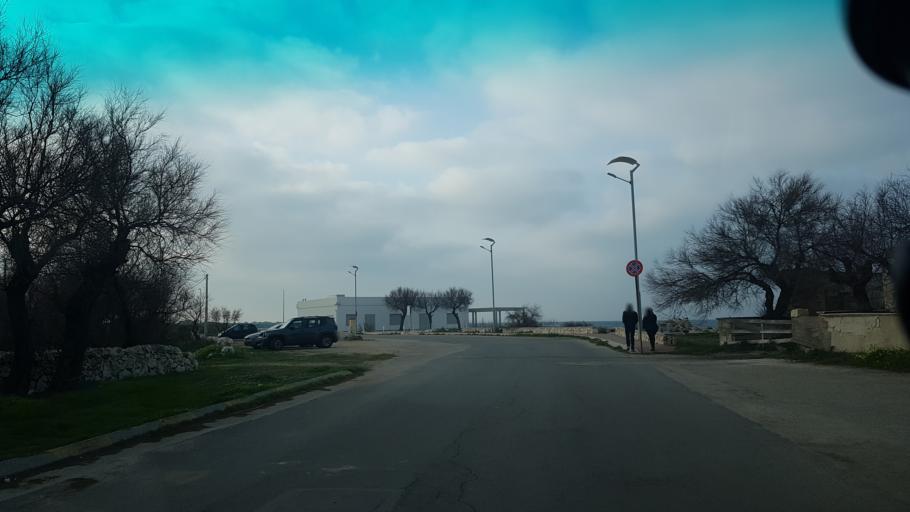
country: IT
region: Apulia
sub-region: Provincia di Brindisi
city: Carovigno
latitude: 40.7442
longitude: 17.7348
